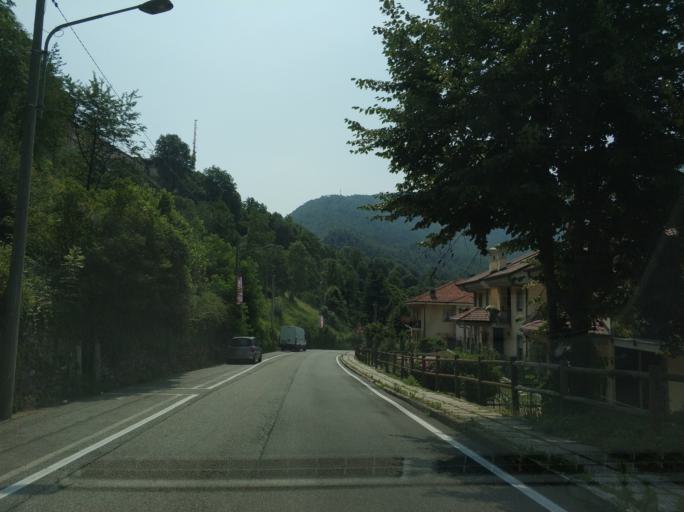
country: IT
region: Piedmont
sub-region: Provincia di Torino
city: Lanzo Torinese
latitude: 45.2719
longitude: 7.4761
